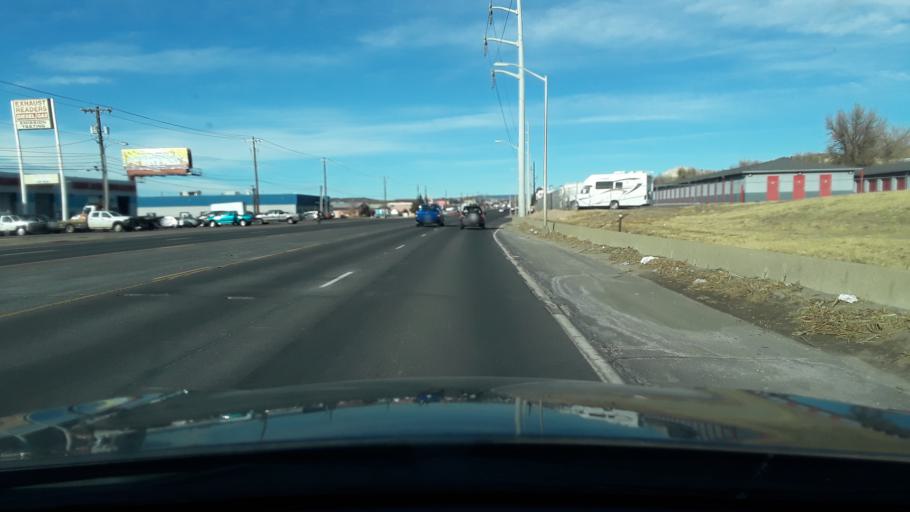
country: US
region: Colorado
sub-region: El Paso County
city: Colorado Springs
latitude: 38.8917
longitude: -104.8190
